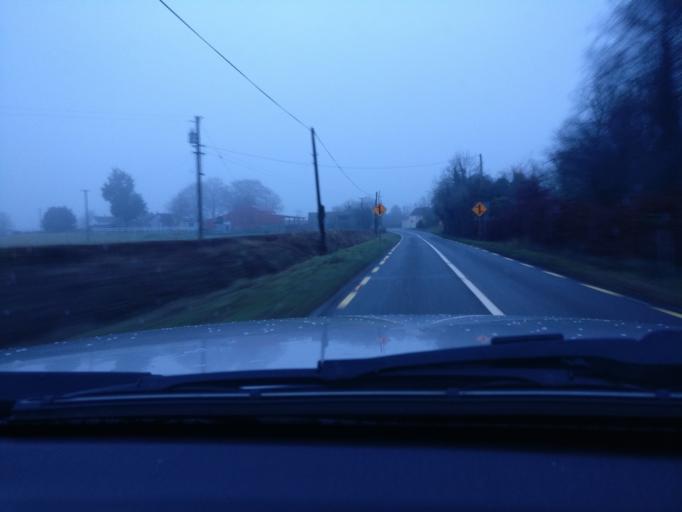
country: IE
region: Leinster
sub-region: An Mhi
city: Athboy
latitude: 53.6043
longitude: -6.9828
